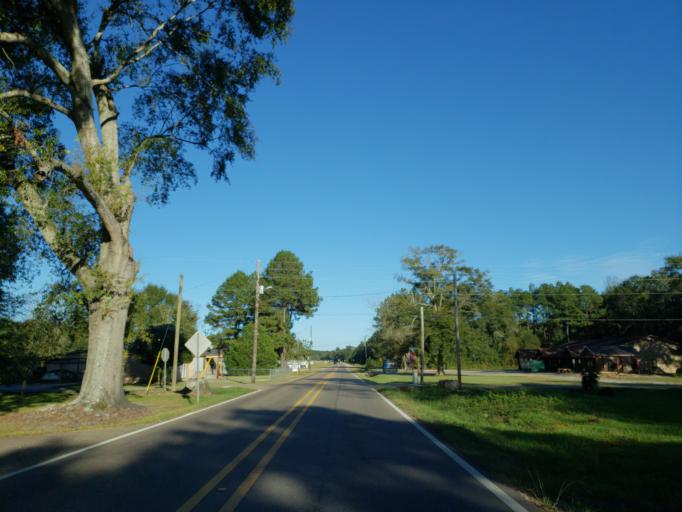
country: US
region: Mississippi
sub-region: Perry County
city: Richton
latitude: 31.3548
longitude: -88.9336
